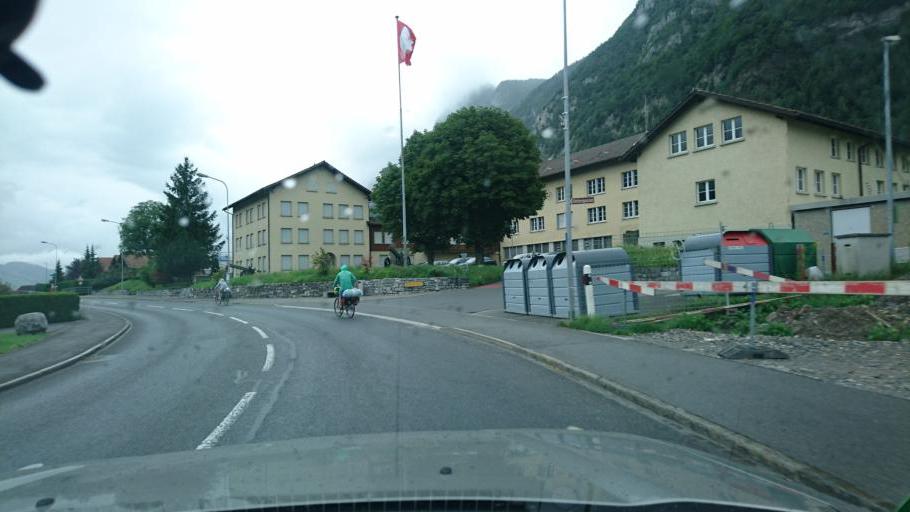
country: CH
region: Saint Gallen
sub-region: Wahlkreis Sarganserland
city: Sargans
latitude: 47.0592
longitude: 9.4109
